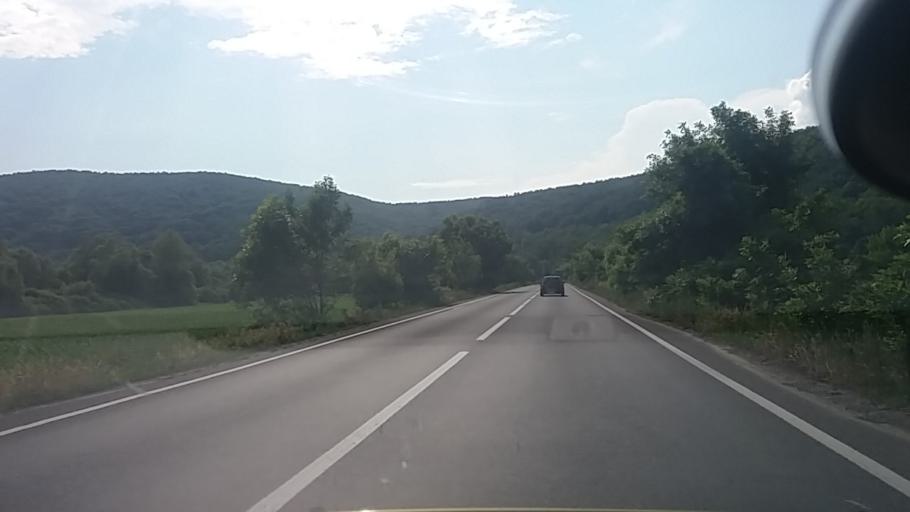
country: RO
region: Arad
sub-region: Comuna Barzava
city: Barzava
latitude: 46.1133
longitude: 21.9601
